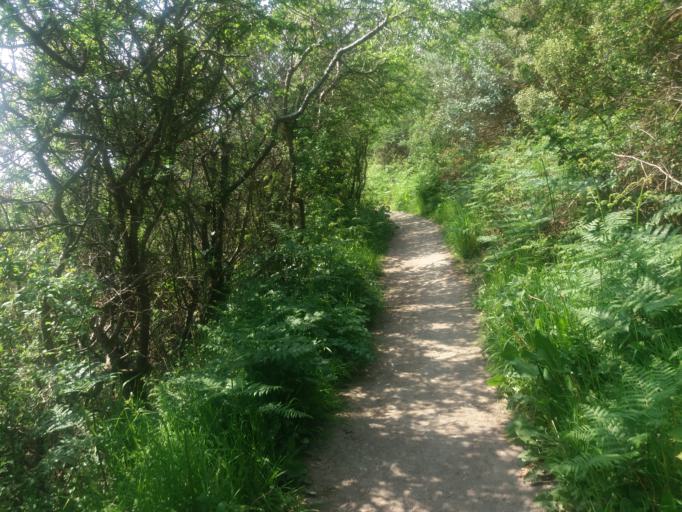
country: IE
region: Leinster
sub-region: Fingal County
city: Howth
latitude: 53.3649
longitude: -6.0695
